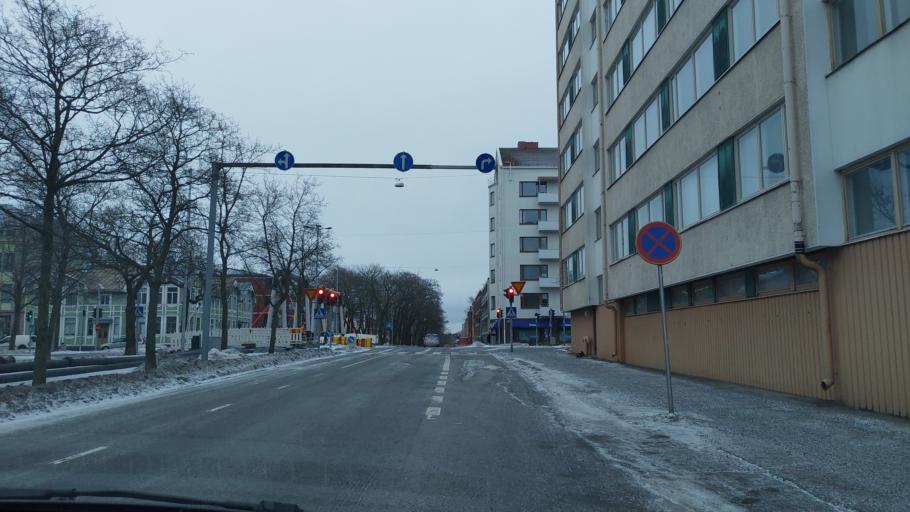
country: FI
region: Ostrobothnia
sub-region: Vaasa
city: Vaasa
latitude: 63.0903
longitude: 21.6194
